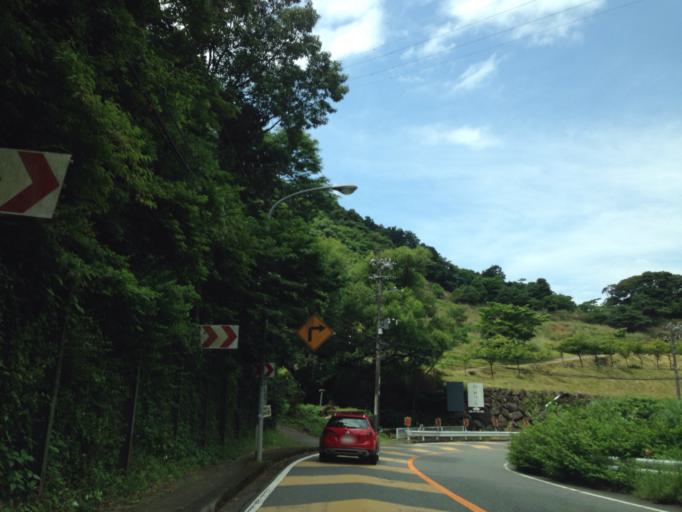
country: JP
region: Shizuoka
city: Heda
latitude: 34.9052
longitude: 138.8130
